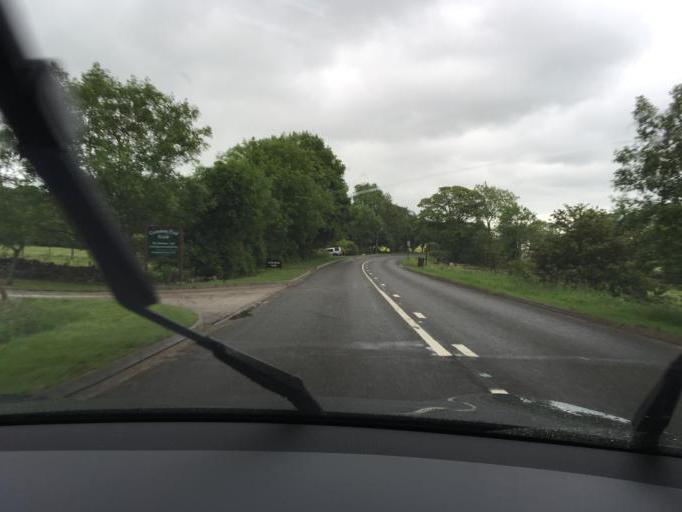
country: GB
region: England
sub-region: Staffordshire
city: Mayfield
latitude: 53.0341
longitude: -1.8105
